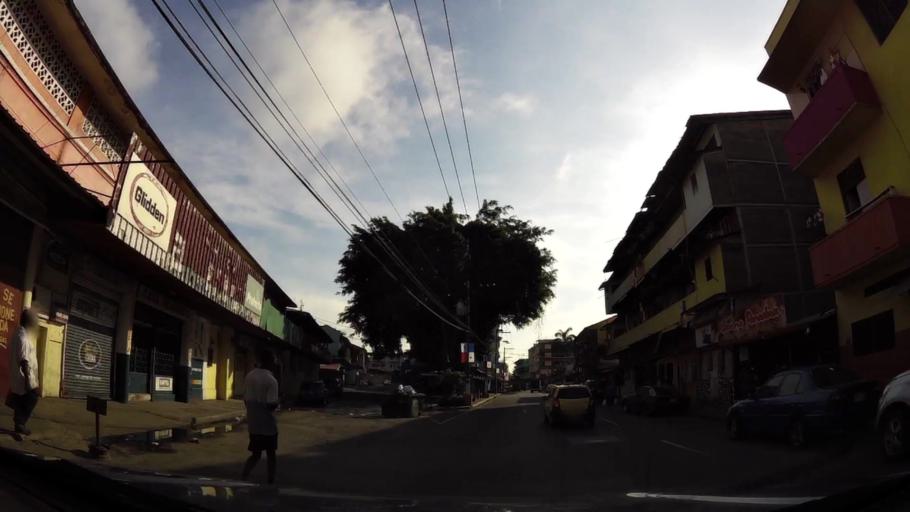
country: PA
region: Panama
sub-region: Distrito de Panama
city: Ancon
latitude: 8.9516
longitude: -79.5421
